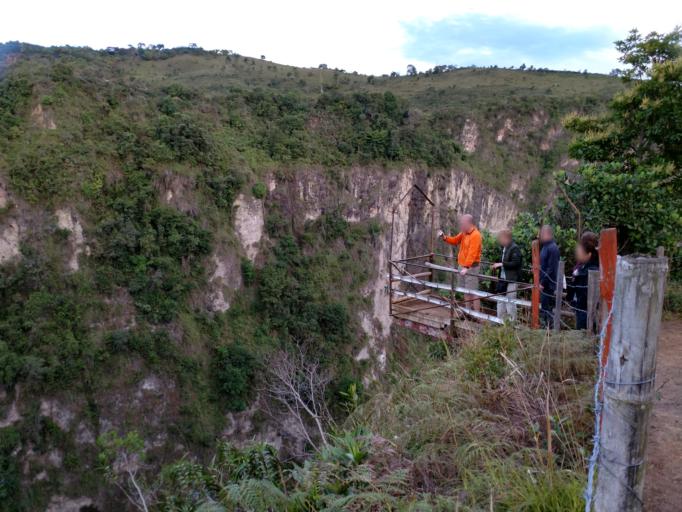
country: CO
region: Huila
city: Isnos
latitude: 1.8782
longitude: -76.2043
